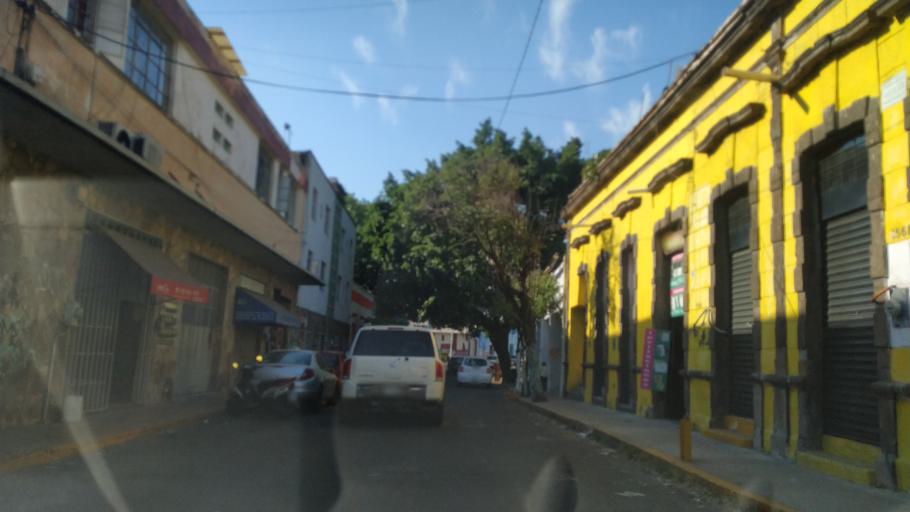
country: MX
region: Jalisco
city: Guadalajara
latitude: 20.6700
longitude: -103.3509
